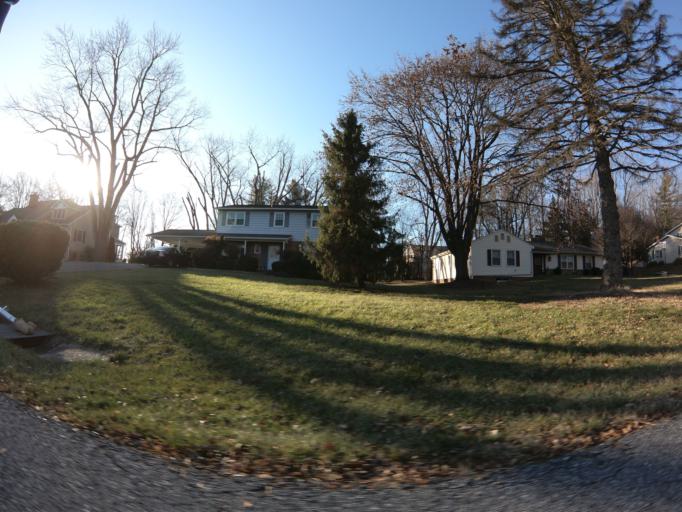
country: US
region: Maryland
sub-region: Howard County
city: Columbia
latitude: 39.2496
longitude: -76.8646
